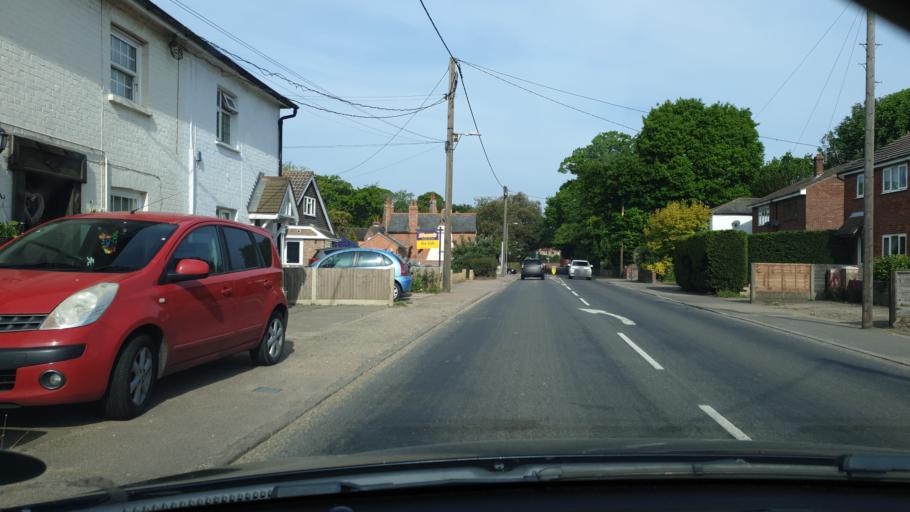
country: GB
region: England
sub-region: Essex
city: Little Clacton
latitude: 51.8556
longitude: 1.1674
